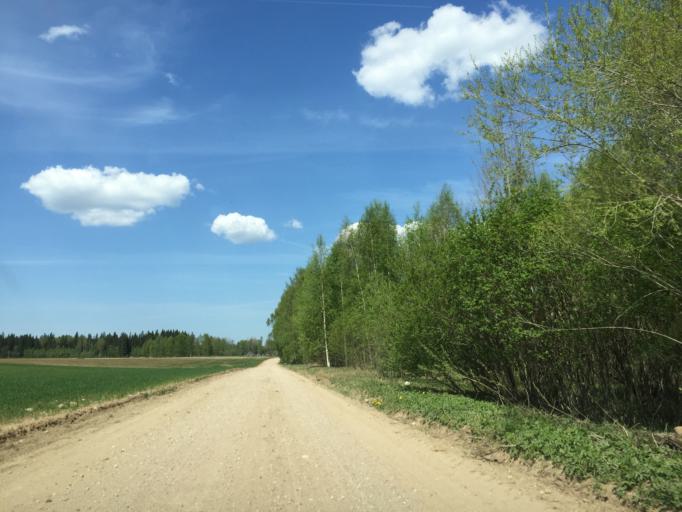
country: LV
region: Limbazu Rajons
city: Limbazi
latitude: 57.3598
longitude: 24.6410
